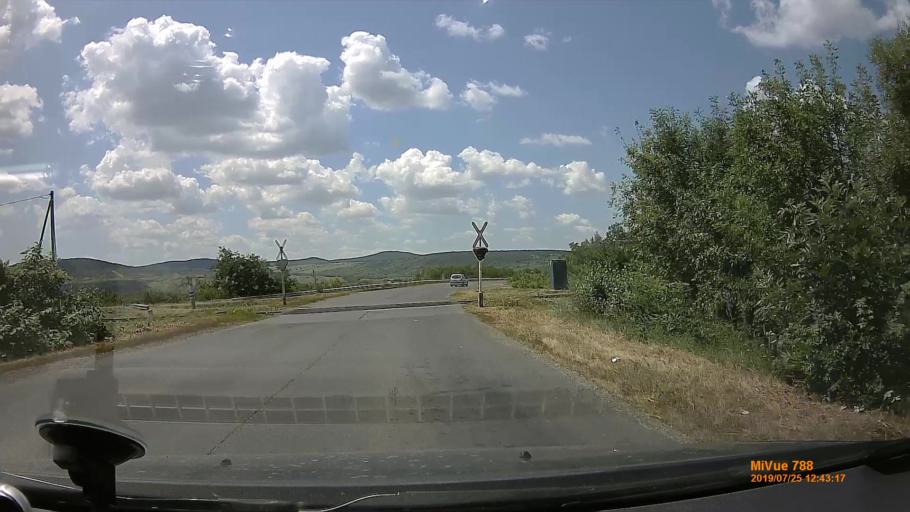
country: HU
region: Borsod-Abauj-Zemplen
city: Tallya
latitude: 48.2250
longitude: 21.2274
